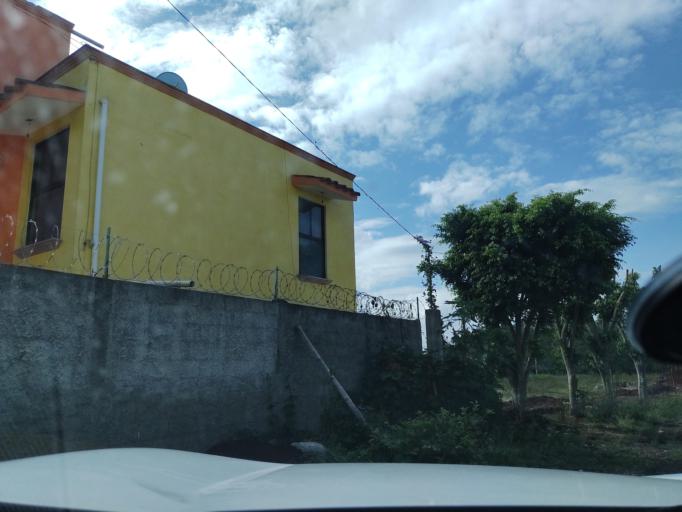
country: MX
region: Veracruz
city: Coatepec
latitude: 19.4814
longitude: -96.9318
